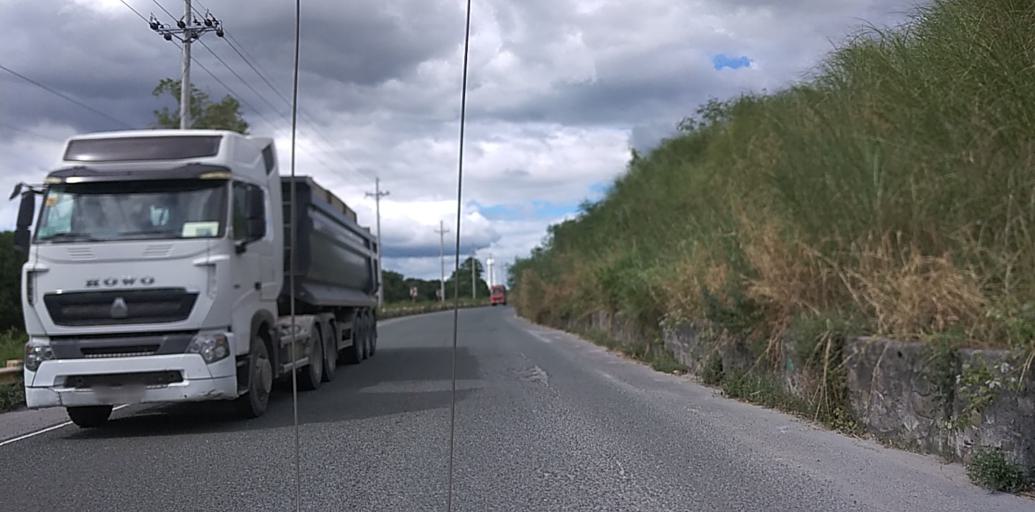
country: PH
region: Central Luzon
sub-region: Province of Pampanga
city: Dolores
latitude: 15.1054
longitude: 120.5211
